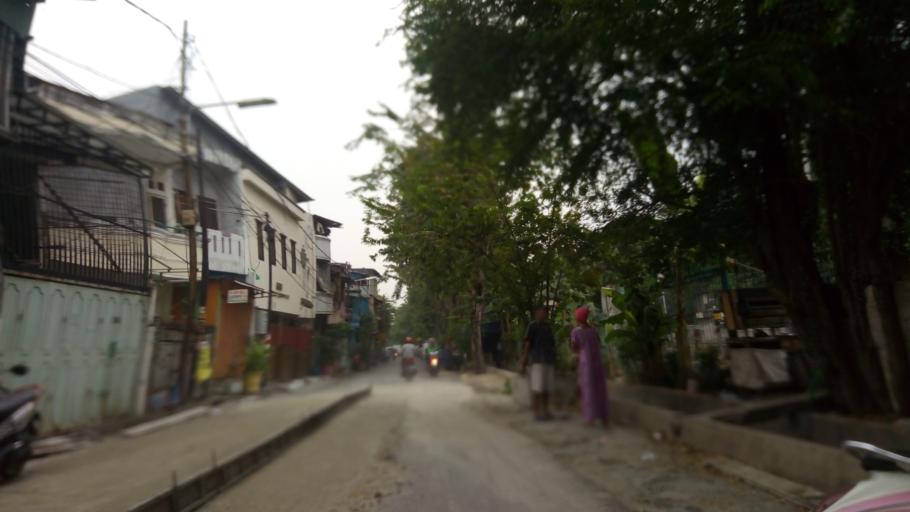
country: ID
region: Jakarta Raya
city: Jakarta
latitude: -6.1530
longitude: 106.8390
